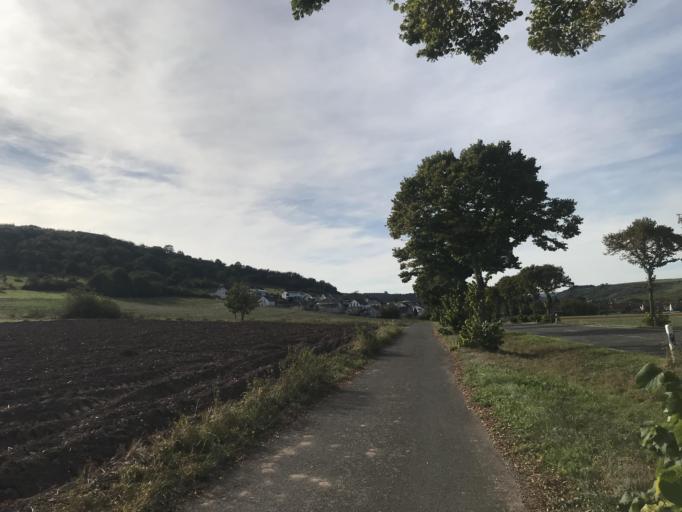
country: DE
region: Rheinland-Pfalz
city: Merxheim
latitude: 49.7916
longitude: 7.5738
